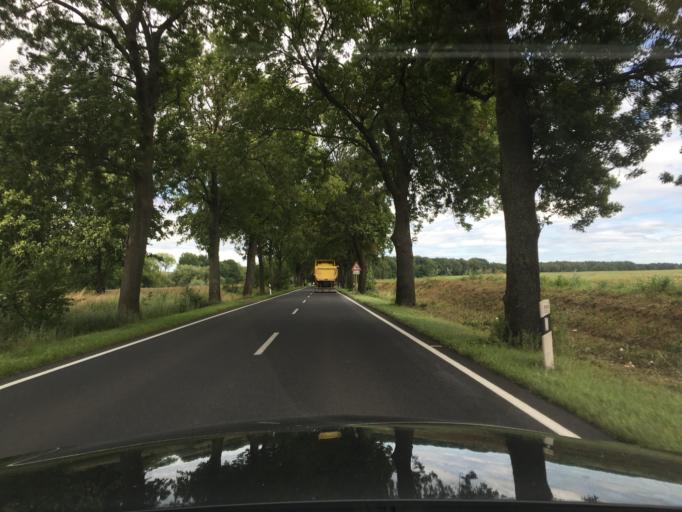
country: DE
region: Brandenburg
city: Gransee
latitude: 52.9070
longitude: 13.1579
